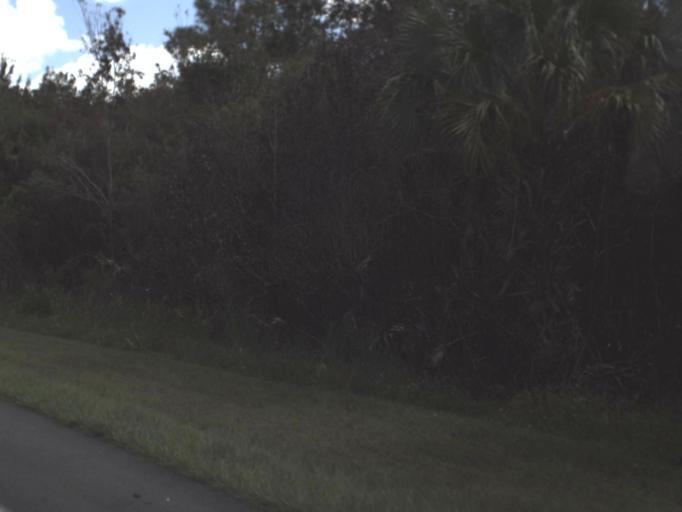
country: US
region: Florida
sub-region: Collier County
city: Marco
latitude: 25.8772
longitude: -81.2329
